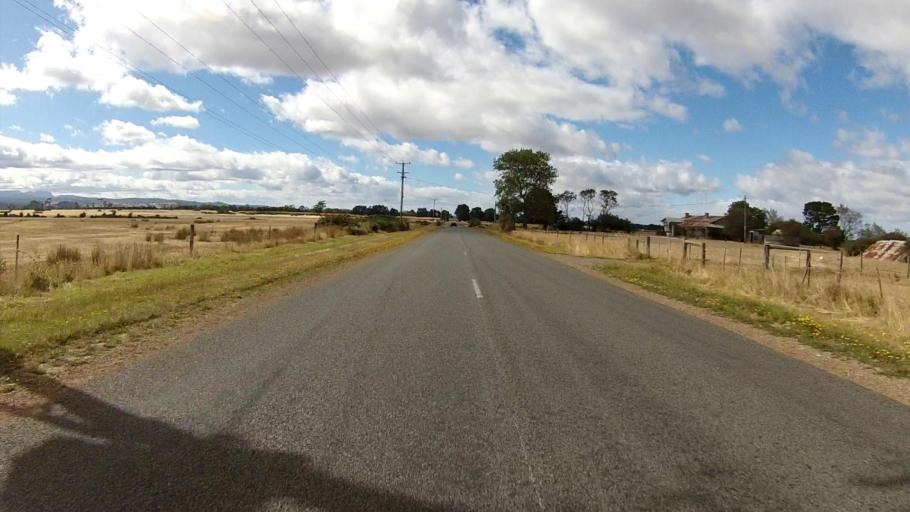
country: AU
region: Tasmania
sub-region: Northern Midlands
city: Evandale
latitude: -41.5976
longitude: 147.2727
